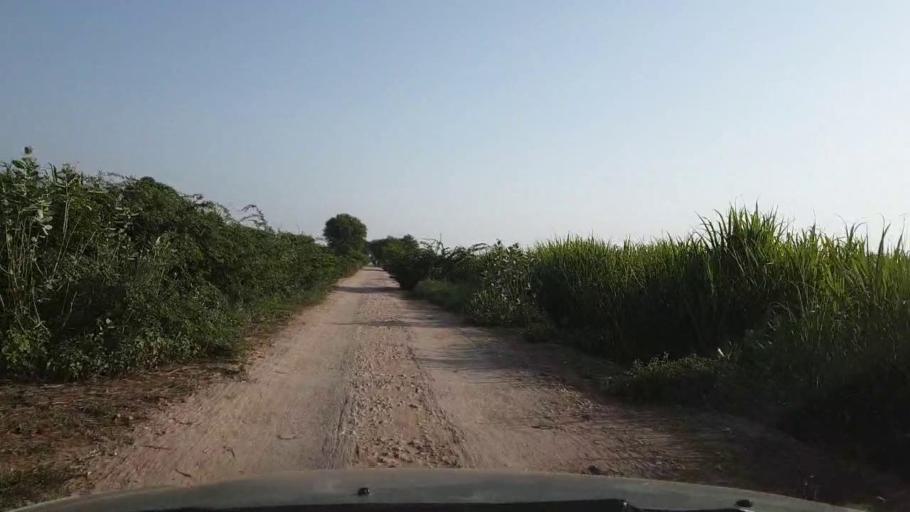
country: PK
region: Sindh
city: Tando Ghulam Ali
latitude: 25.1369
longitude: 68.9408
